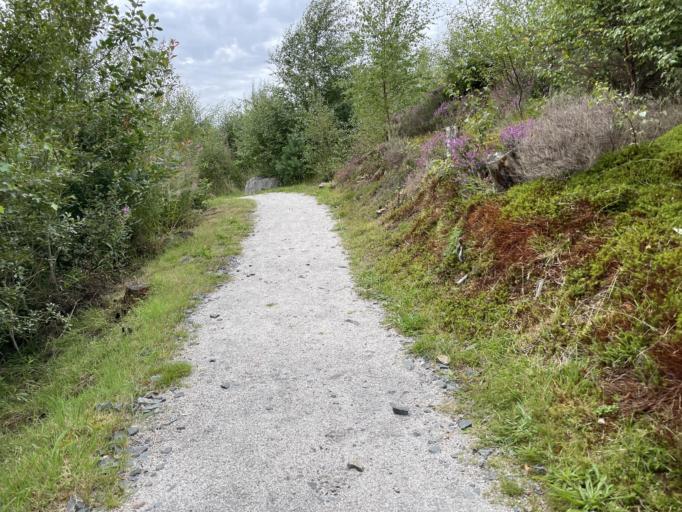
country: GB
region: Scotland
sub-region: Dumfries and Galloway
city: Newton Stewart
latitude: 55.0844
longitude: -4.5033
